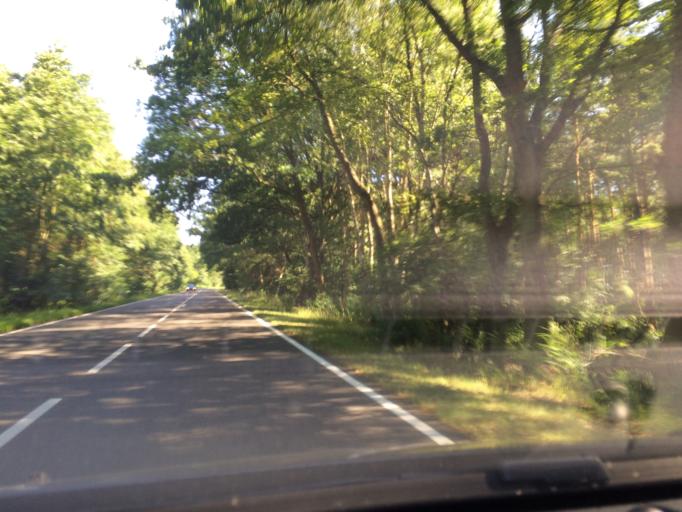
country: DE
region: Mecklenburg-Vorpommern
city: Zingst
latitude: 54.4371
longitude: 12.6503
